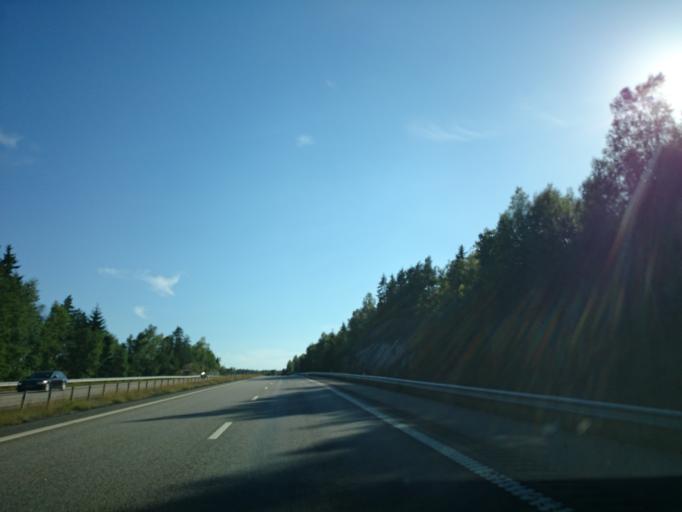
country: SE
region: Soedermanland
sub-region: Gnesta Kommun
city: Gnesta
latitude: 58.8620
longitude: 17.2176
